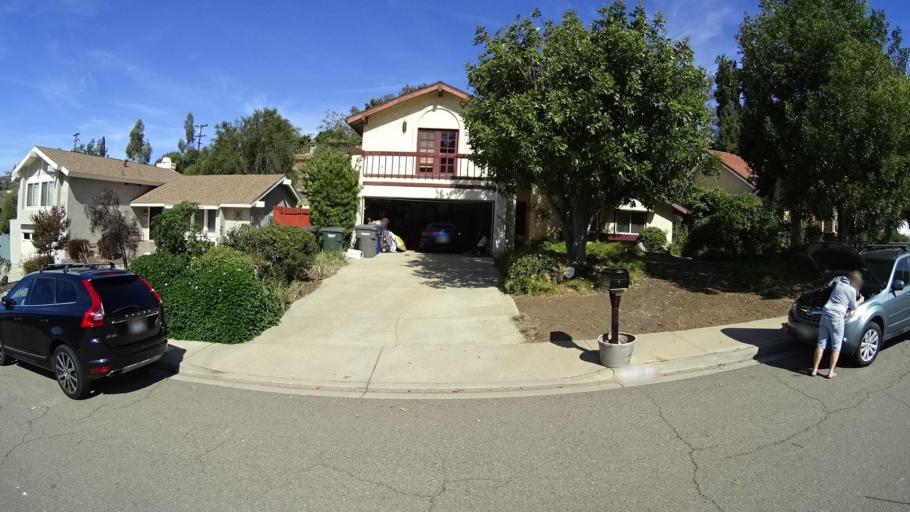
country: US
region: California
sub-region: San Diego County
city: Casa de Oro-Mount Helix
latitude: 32.7547
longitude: -116.9586
